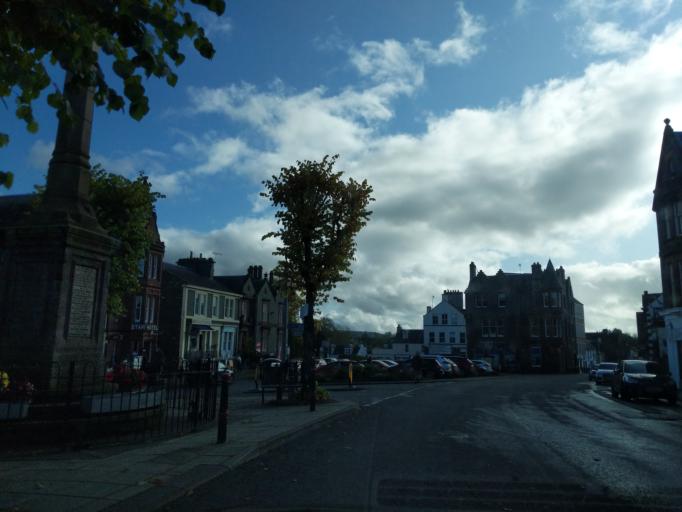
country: GB
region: Scotland
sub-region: Dumfries and Galloway
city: Moffat
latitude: 55.3329
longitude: -3.4442
